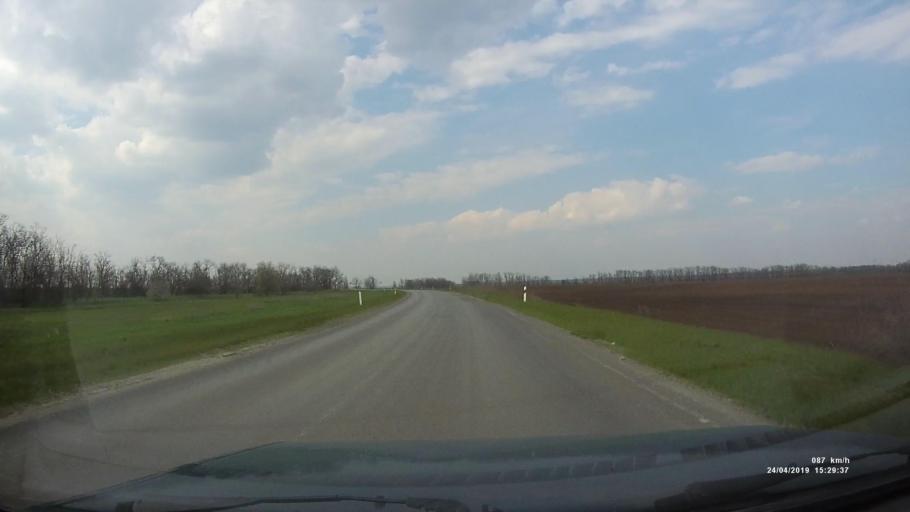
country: RU
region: Rostov
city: Remontnoye
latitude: 46.5953
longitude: 43.0171
